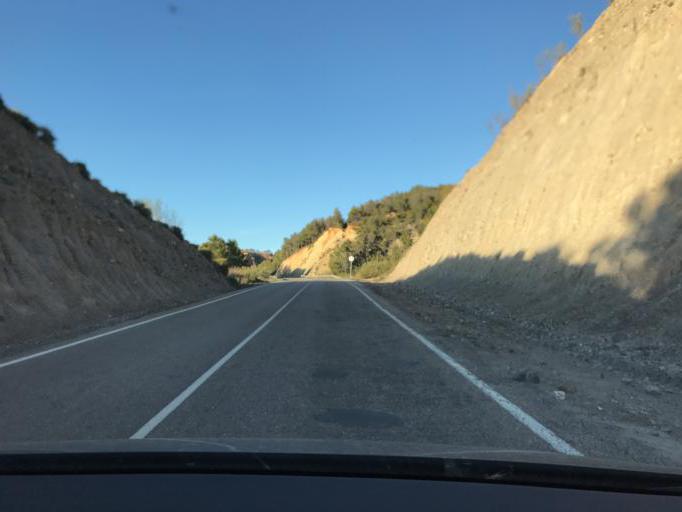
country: ES
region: Andalusia
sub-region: Provincia de Granada
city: Policar
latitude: 37.2861
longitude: -3.2750
